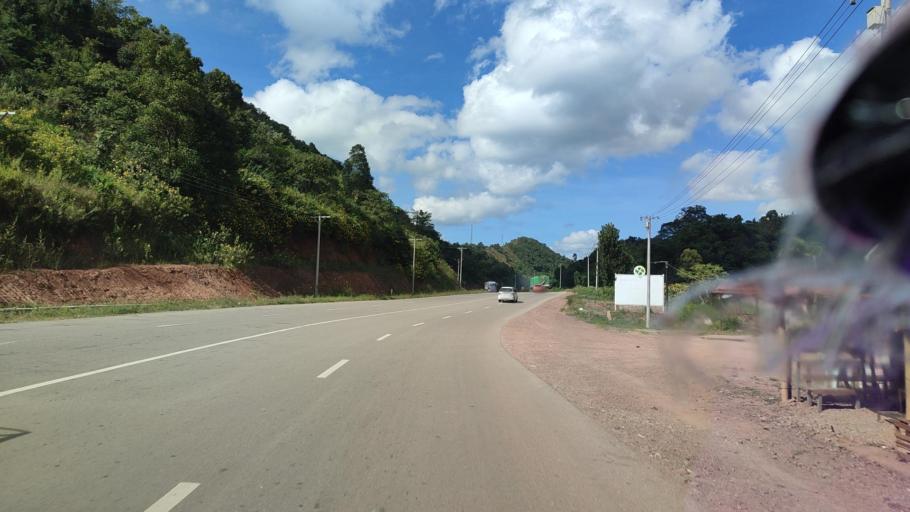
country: MM
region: Mandalay
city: Yamethin
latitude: 20.6673
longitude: 96.5340
